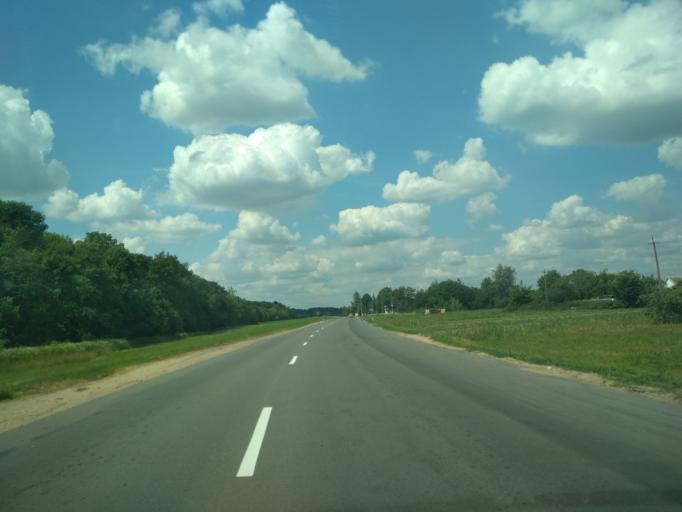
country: BY
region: Minsk
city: Druzhny
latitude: 53.5730
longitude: 27.9413
